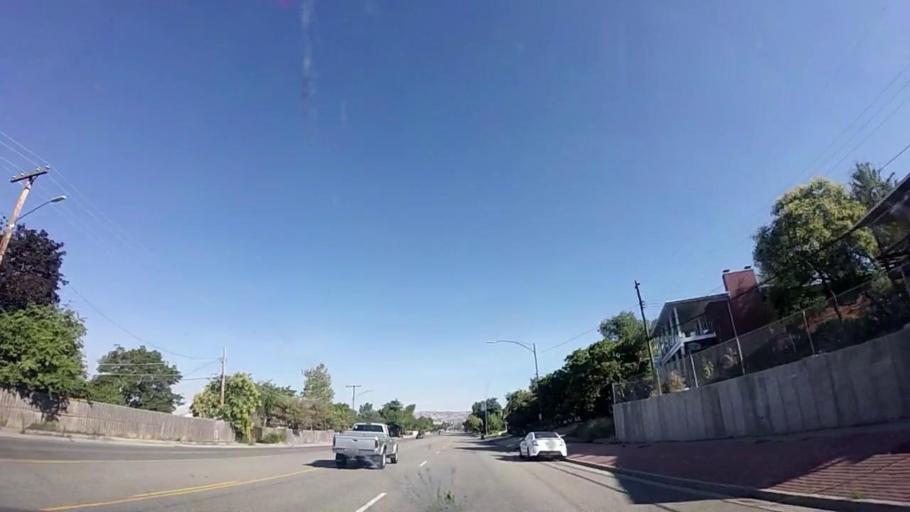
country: US
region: Utah
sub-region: Salt Lake County
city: Canyon Rim
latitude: 40.7285
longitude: -111.8166
